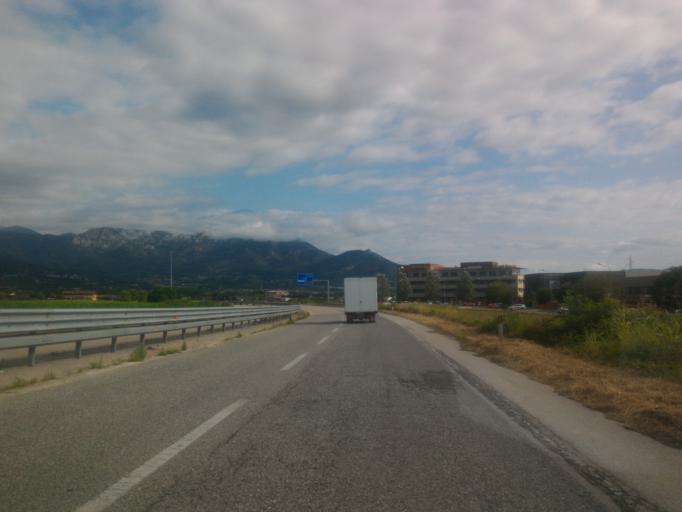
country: IT
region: Piedmont
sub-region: Provincia di Torino
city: Riva
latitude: 44.8989
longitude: 7.3609
